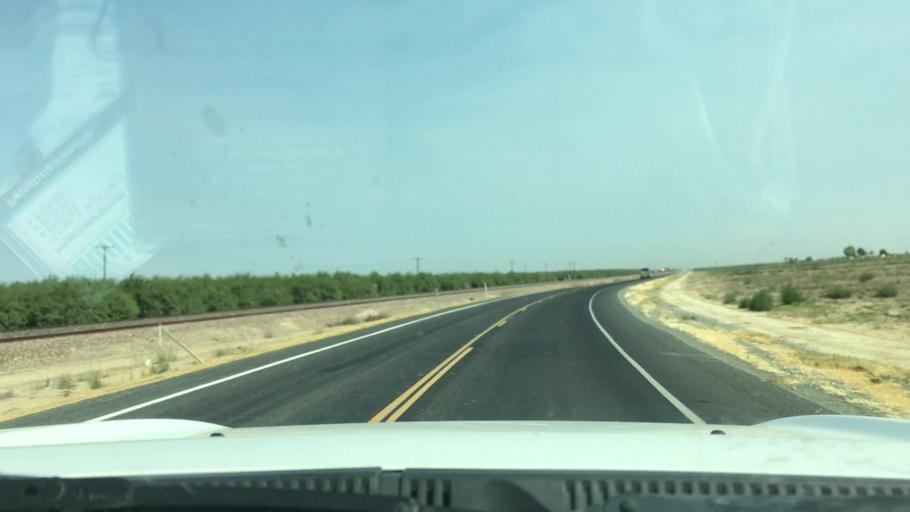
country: US
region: California
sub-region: Kern County
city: Delano
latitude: 35.7641
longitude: -119.3460
